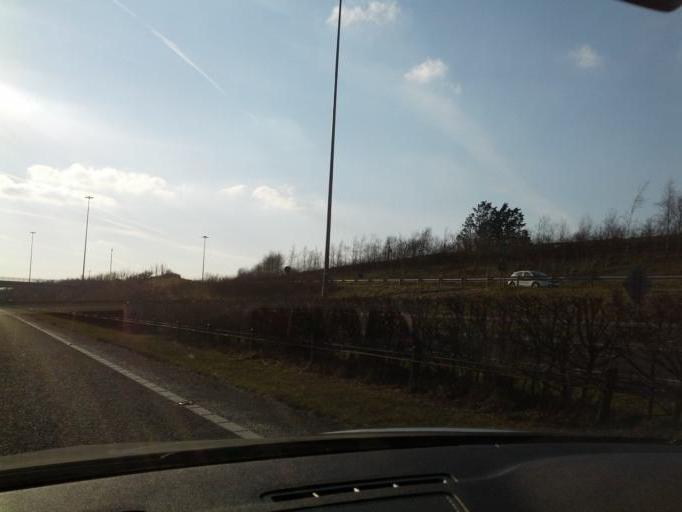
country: IE
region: Leinster
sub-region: Kildare
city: Cherryville
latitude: 53.1465
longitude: -7.0111
